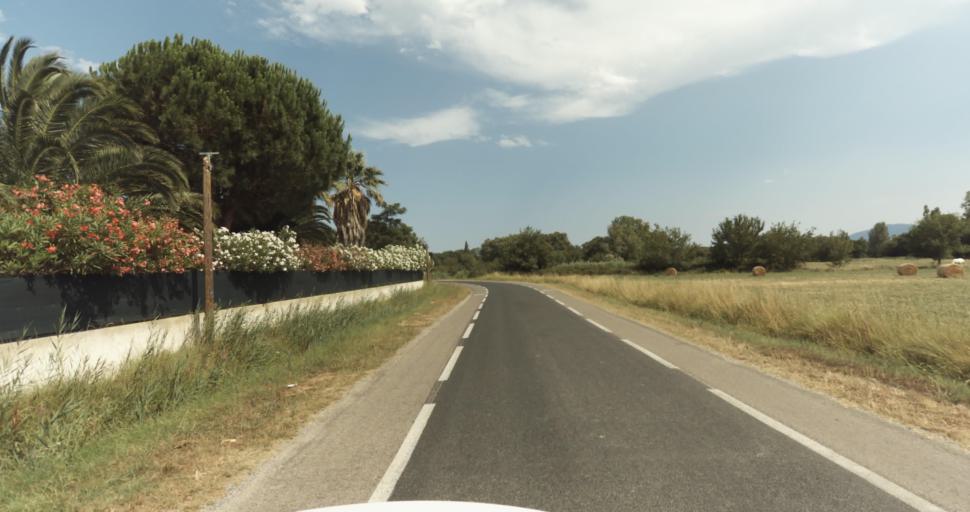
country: FR
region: Languedoc-Roussillon
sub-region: Departement des Pyrenees-Orientales
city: Saint-Cyprien-Plage
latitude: 42.6302
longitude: 3.0128
